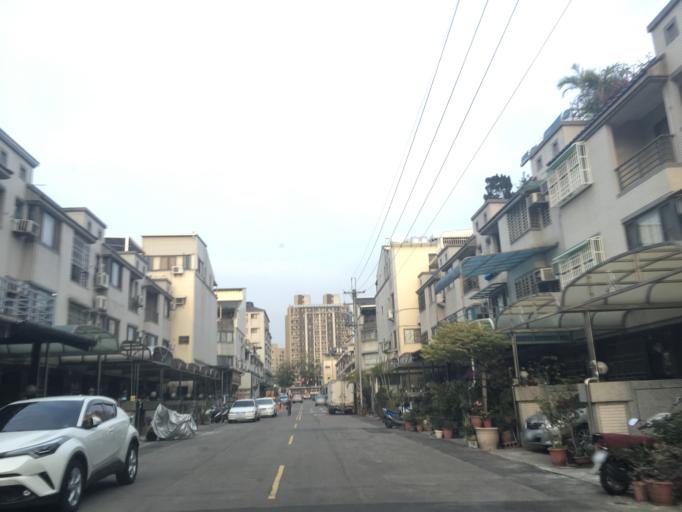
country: TW
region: Taiwan
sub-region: Taichung City
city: Taichung
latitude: 24.1754
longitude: 120.7078
